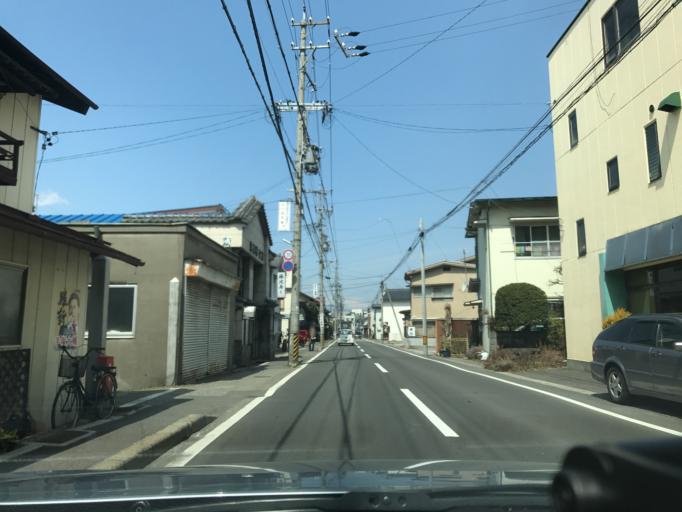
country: JP
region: Nagano
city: Matsumoto
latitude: 36.2332
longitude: 137.9612
